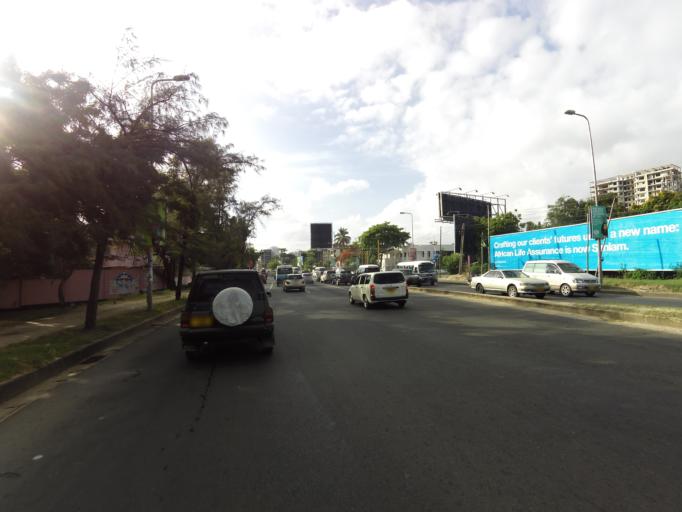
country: TZ
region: Dar es Salaam
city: Dar es Salaam
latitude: -6.7967
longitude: 39.2817
